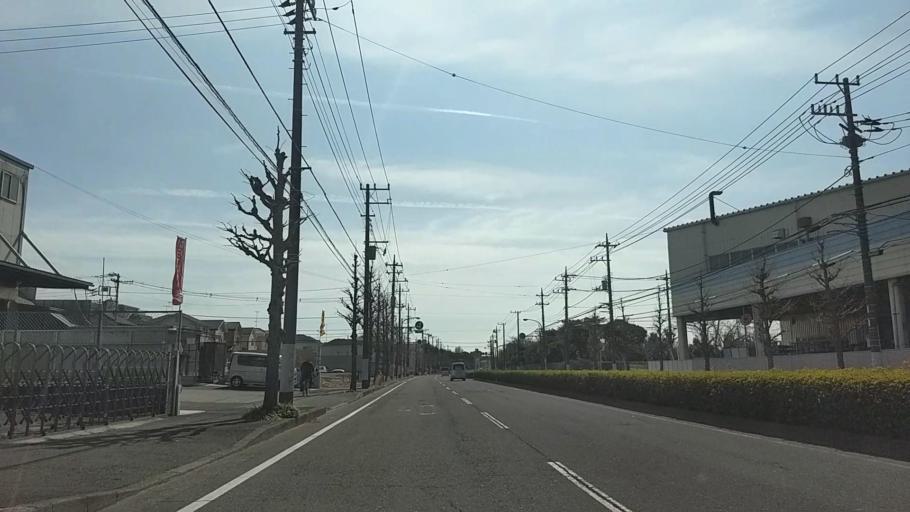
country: JP
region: Kanagawa
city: Fujisawa
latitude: 35.3880
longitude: 139.4574
